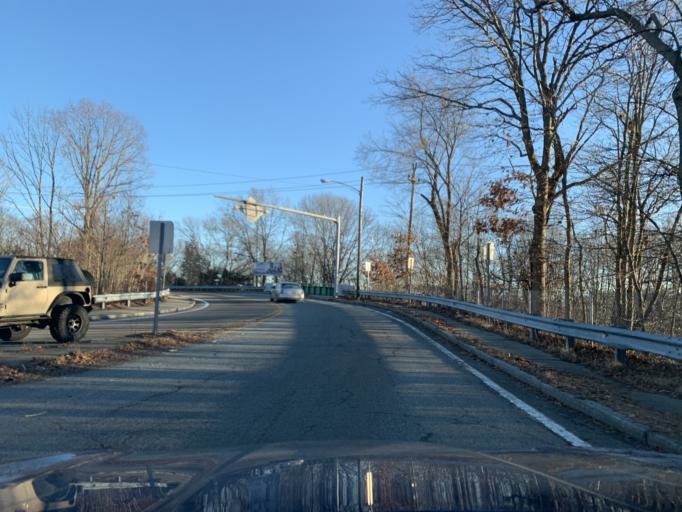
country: US
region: Rhode Island
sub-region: Kent County
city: West Warwick
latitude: 41.6955
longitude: -71.5346
